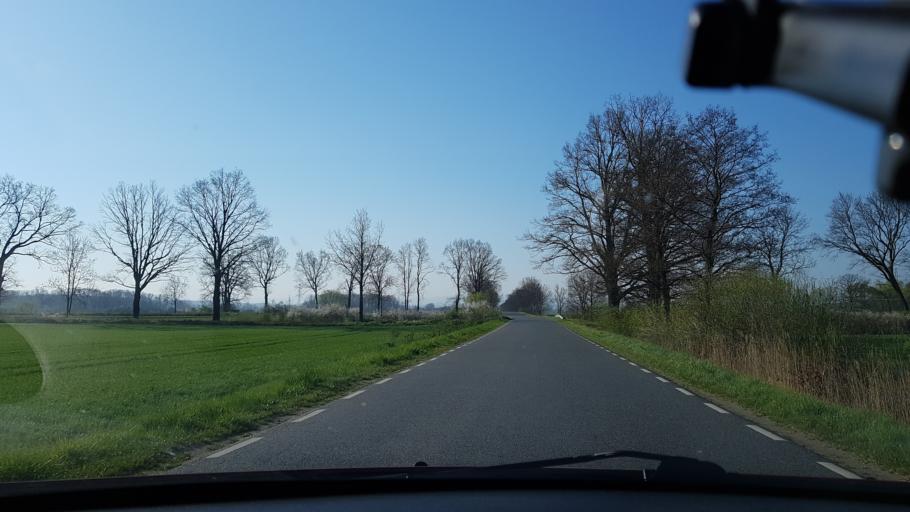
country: PL
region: Opole Voivodeship
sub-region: Powiat nyski
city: Otmuchow
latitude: 50.4420
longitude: 17.1707
